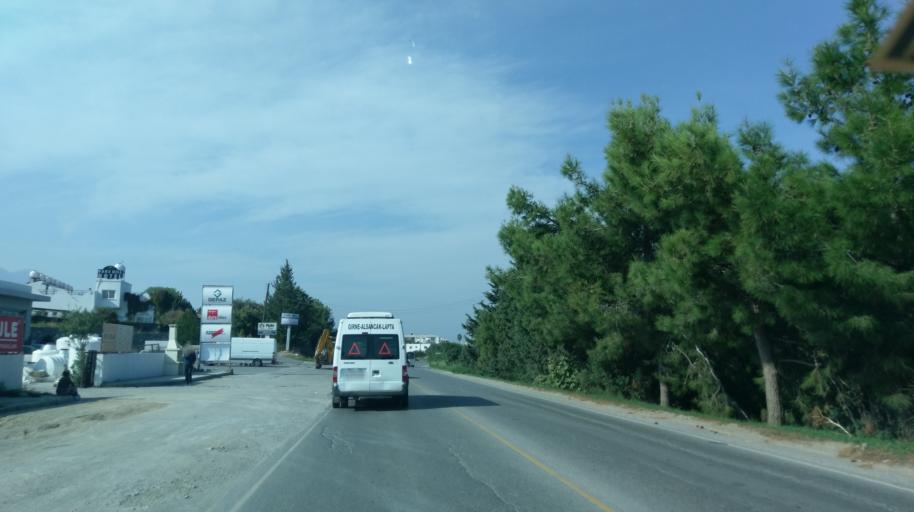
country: CY
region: Keryneia
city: Lapithos
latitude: 35.3465
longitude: 33.2295
